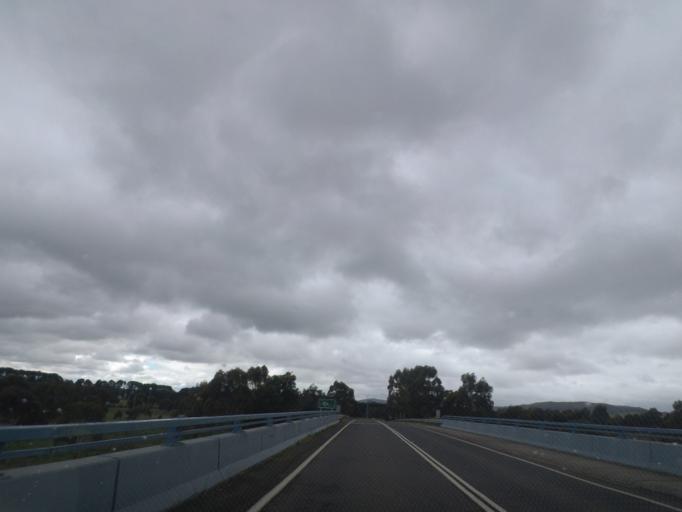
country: AU
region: Victoria
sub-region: Hume
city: Sunbury
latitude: -37.3206
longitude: 144.5260
